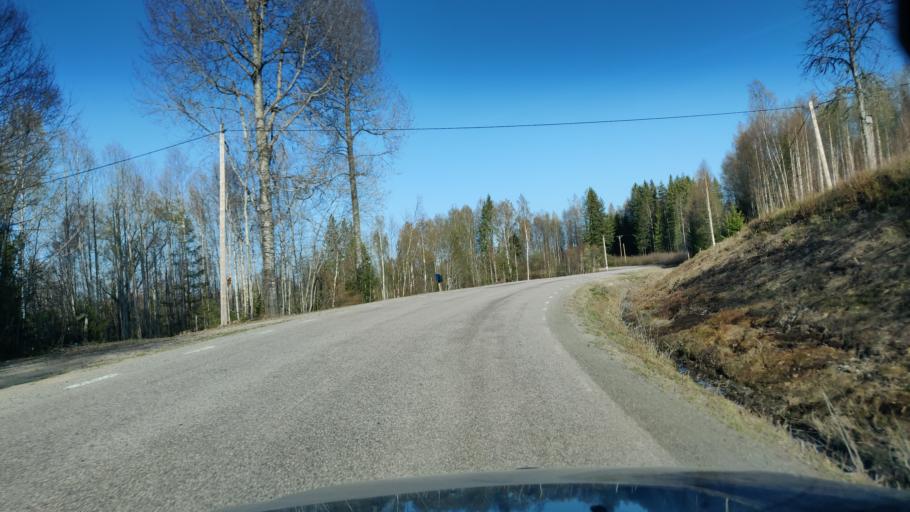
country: SE
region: Vaermland
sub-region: Munkfors Kommun
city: Munkfors
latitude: 59.9705
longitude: 13.4475
